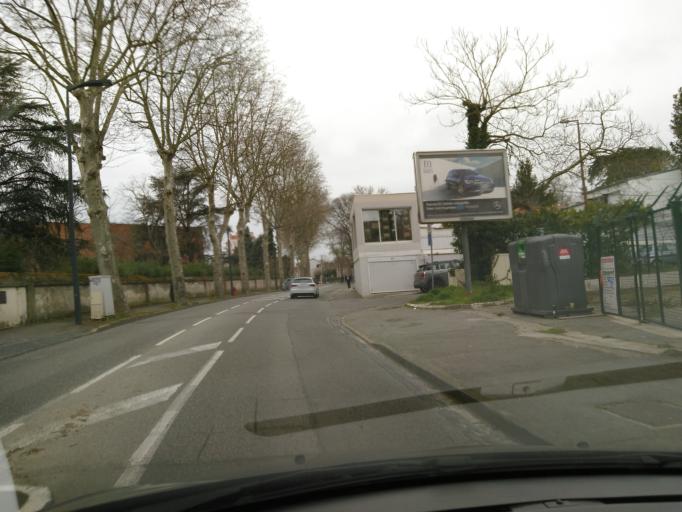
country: FR
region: Midi-Pyrenees
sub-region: Departement de la Haute-Garonne
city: Toulouse
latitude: 43.5927
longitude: 1.4671
